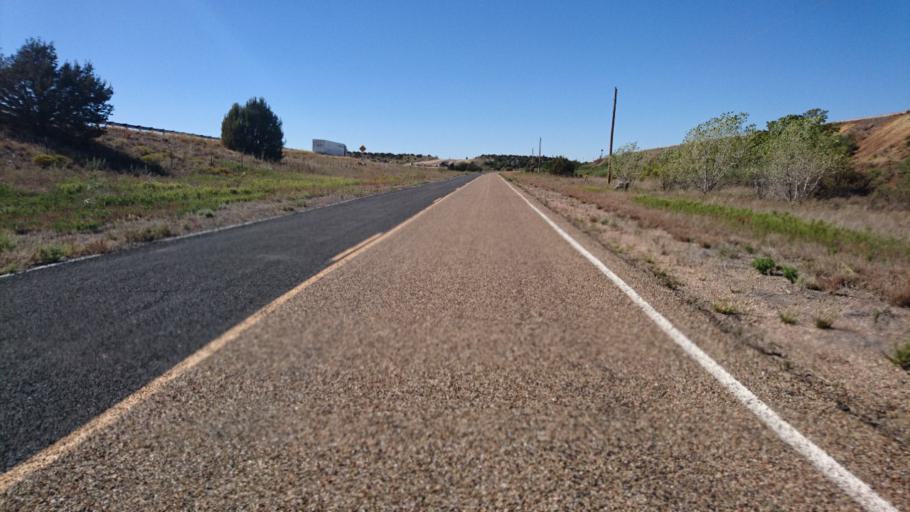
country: US
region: New Mexico
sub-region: Quay County
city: Tucumcari
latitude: 35.0693
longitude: -104.2076
